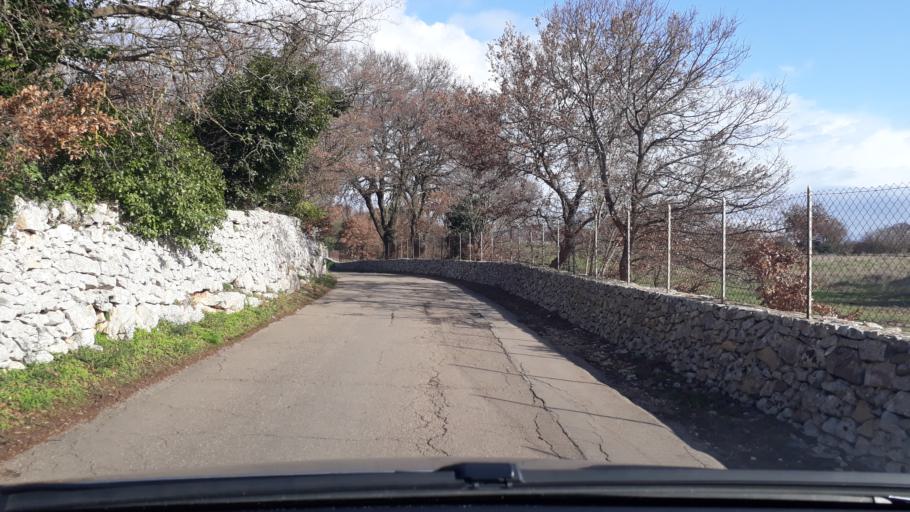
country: IT
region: Apulia
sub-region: Provincia di Brindisi
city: Cisternino
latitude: 40.7044
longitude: 17.4217
